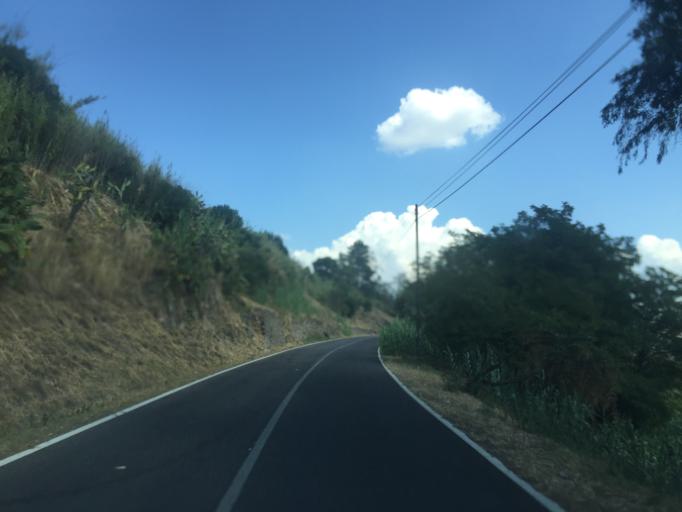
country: PT
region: Santarem
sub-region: Chamusca
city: Vila Nova da Barquinha
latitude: 39.4580
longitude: -8.4177
